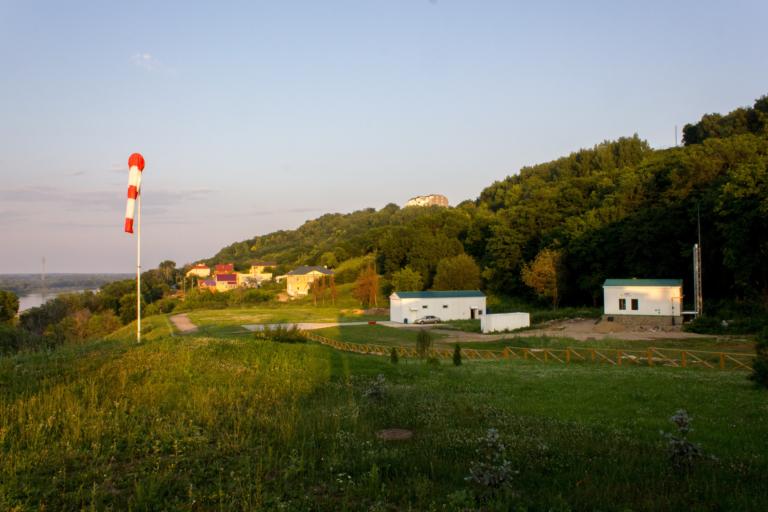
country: RU
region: Nizjnij Novgorod
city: Bor
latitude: 56.3234
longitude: 44.0524
